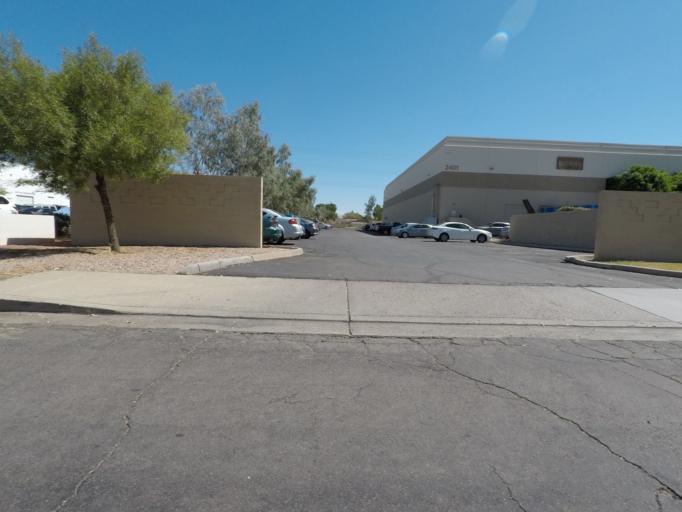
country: US
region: Arizona
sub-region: Maricopa County
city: Tempe Junction
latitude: 33.4031
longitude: -111.9447
